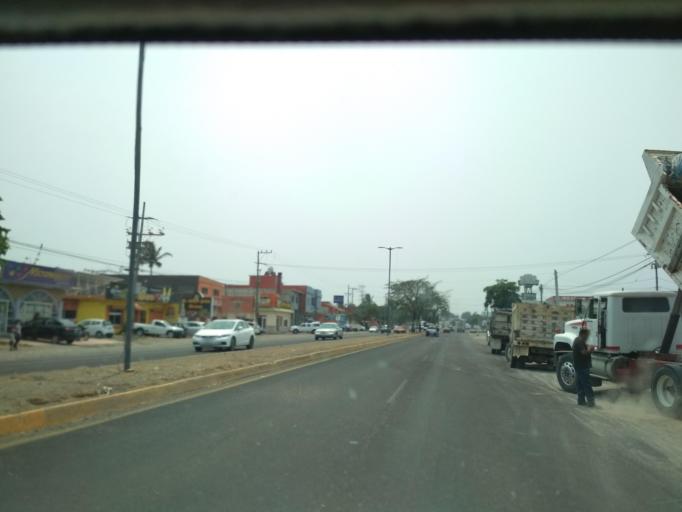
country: MX
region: Veracruz
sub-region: Veracruz
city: Las Amapolas
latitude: 19.1628
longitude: -96.2080
